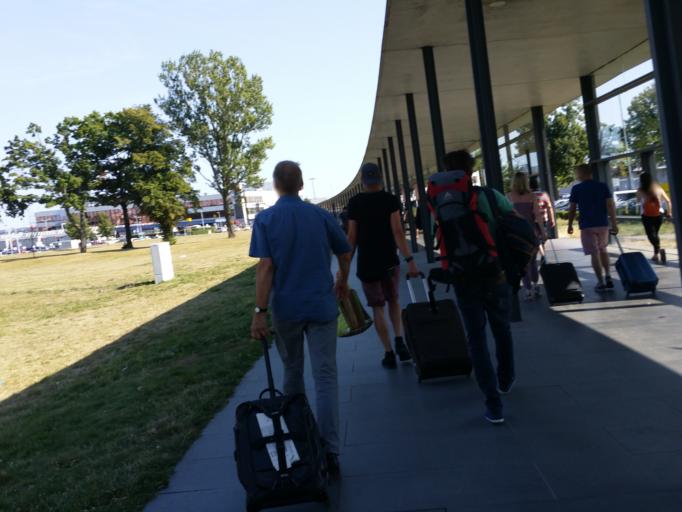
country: DE
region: Brandenburg
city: Schonefeld
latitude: 52.3901
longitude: 13.5152
